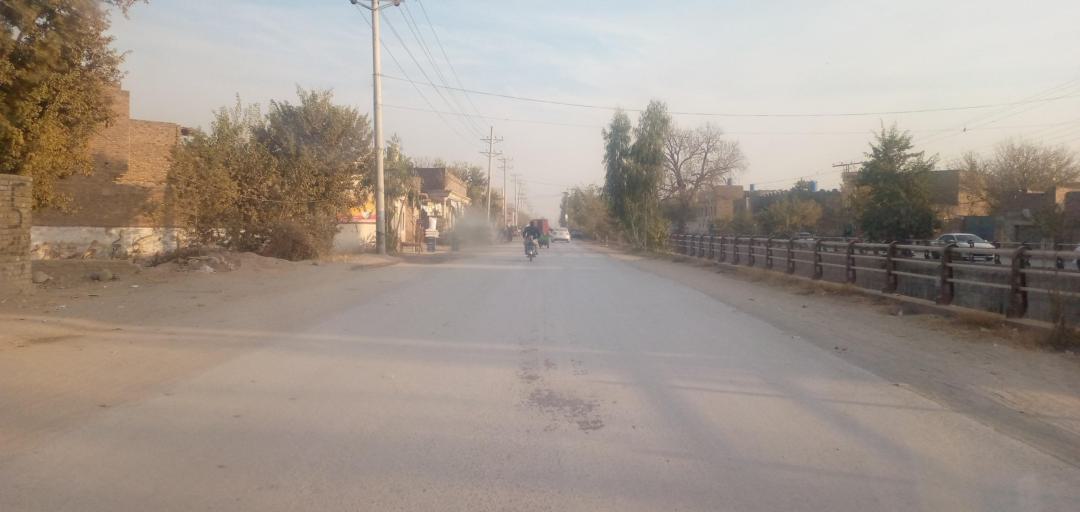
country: PK
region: Khyber Pakhtunkhwa
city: Peshawar
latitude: 33.9725
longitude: 71.5314
